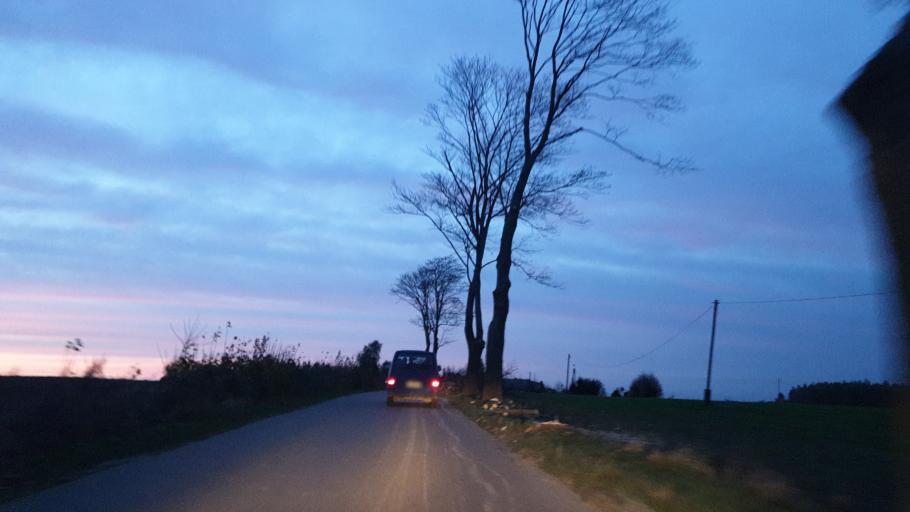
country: PL
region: Pomeranian Voivodeship
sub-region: Powiat pucki
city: Krokowa
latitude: 54.7756
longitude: 18.2095
